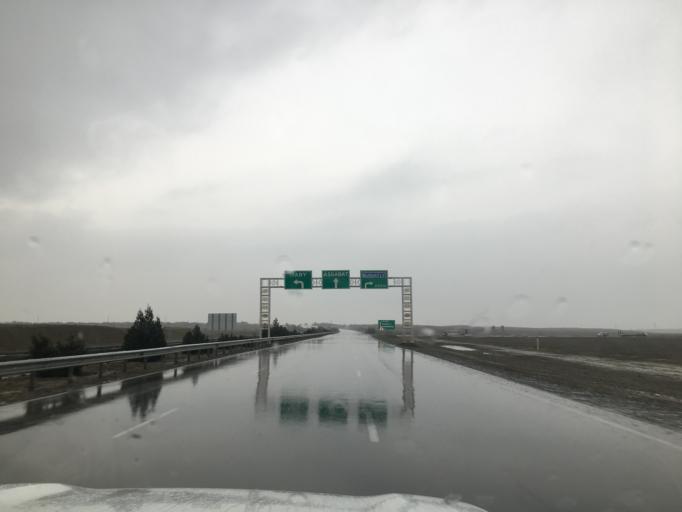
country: TM
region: Ahal
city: Annau
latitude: 37.8439
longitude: 58.7161
